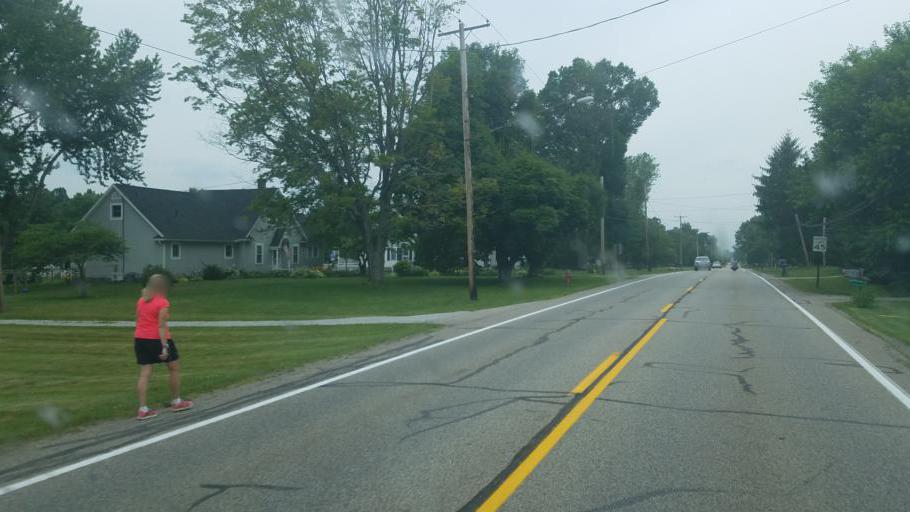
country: US
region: Ohio
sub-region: Portage County
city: Brimfield
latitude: 41.0999
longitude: -81.3332
